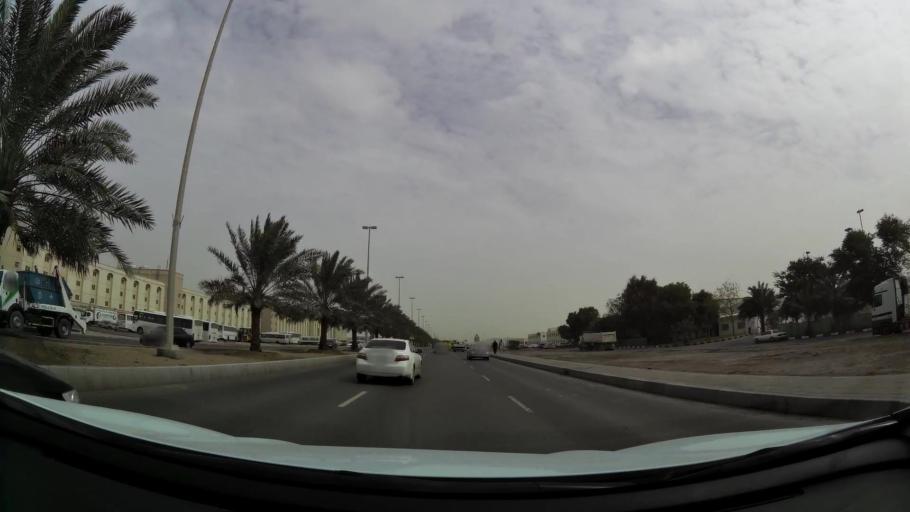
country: AE
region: Abu Dhabi
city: Abu Dhabi
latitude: 24.3459
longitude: 54.5085
